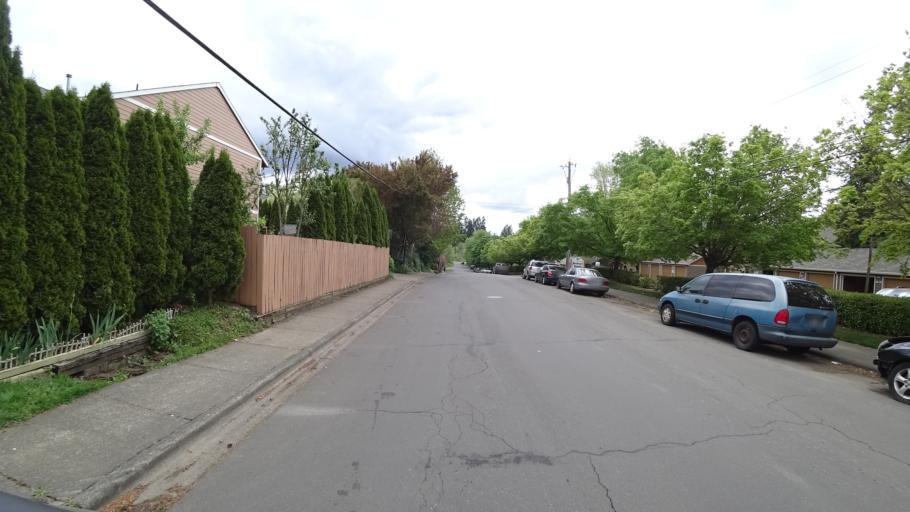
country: US
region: Oregon
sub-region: Washington County
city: Beaverton
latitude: 45.4833
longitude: -122.8299
